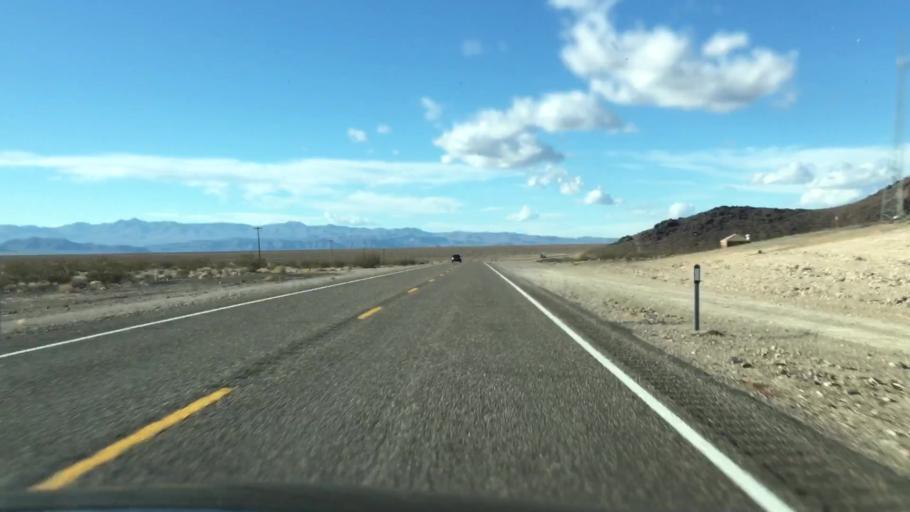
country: US
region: Nevada
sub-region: Nye County
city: Beatty
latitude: 37.1774
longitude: -116.9269
